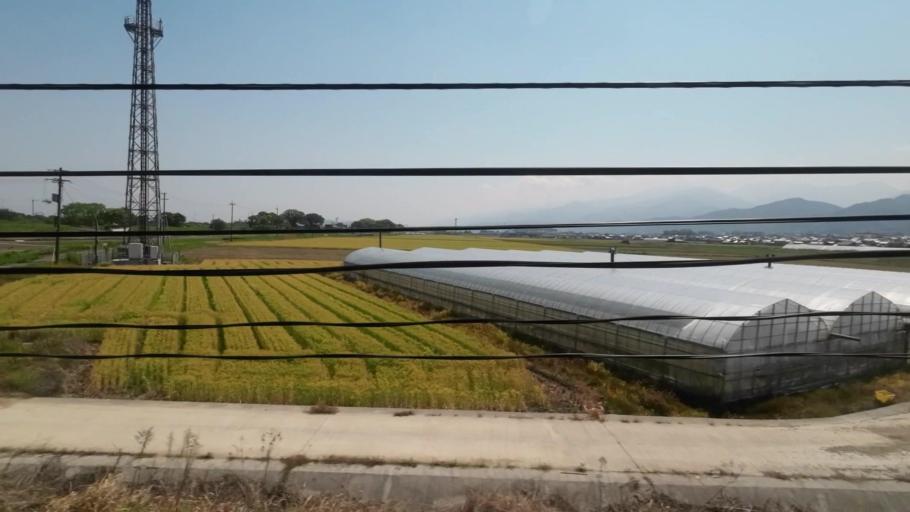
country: JP
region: Ehime
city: Saijo
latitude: 33.9034
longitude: 133.0994
